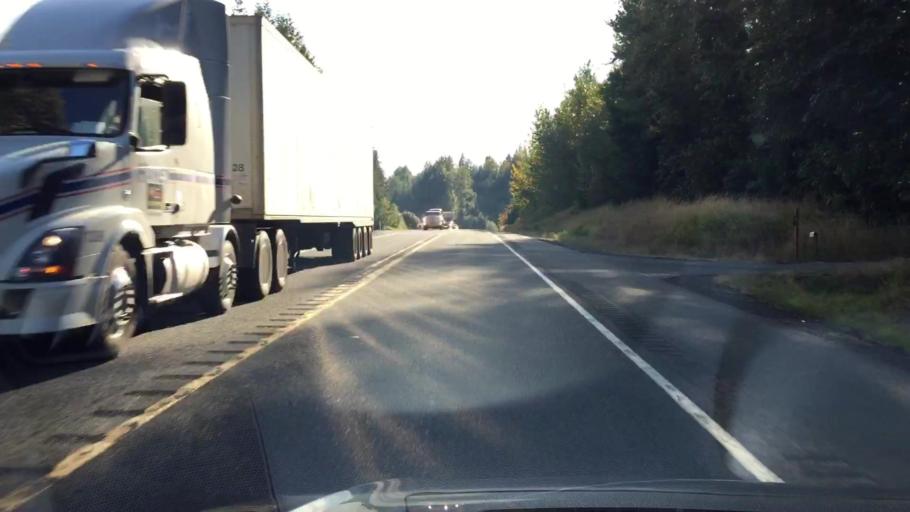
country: US
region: Washington
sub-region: Lewis County
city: Morton
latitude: 46.5146
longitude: -122.1703
